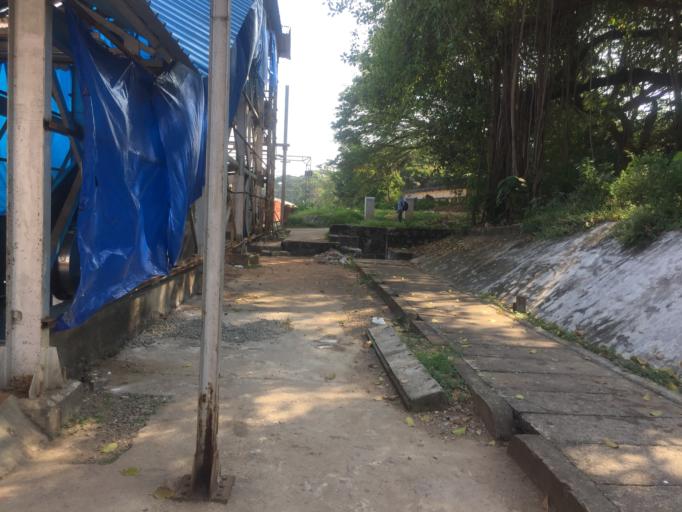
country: IN
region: Karnataka
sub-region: Dakshina Kannada
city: Ullal
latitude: 12.8623
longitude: 74.8431
